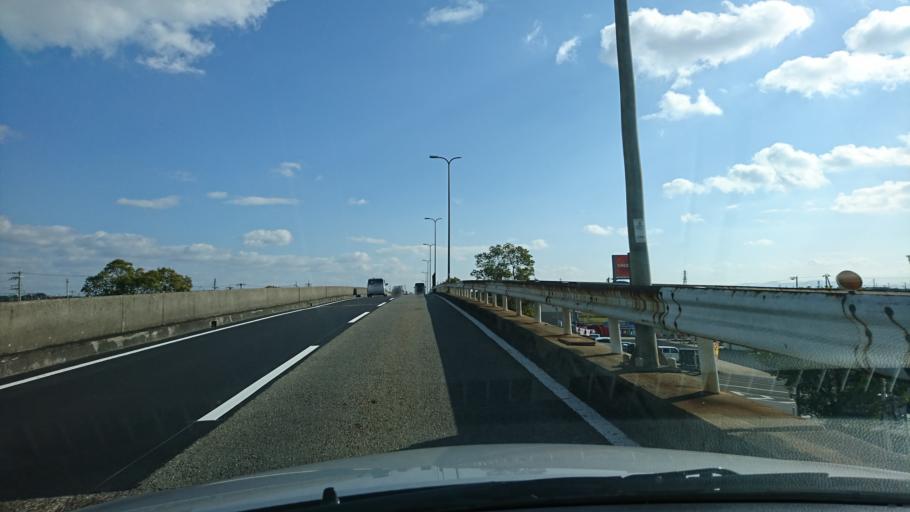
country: JP
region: Hyogo
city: Kakogawacho-honmachi
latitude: 34.7293
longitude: 134.8609
